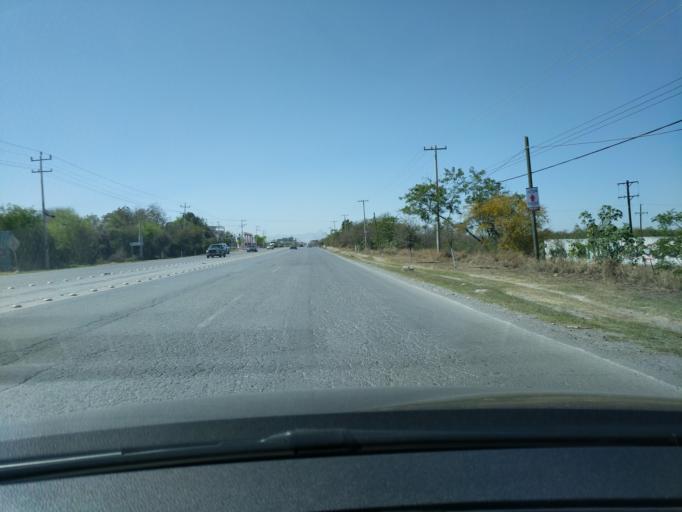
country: MX
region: Nuevo Leon
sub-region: Juarez
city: San Antonio
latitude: 25.6311
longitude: -100.0756
